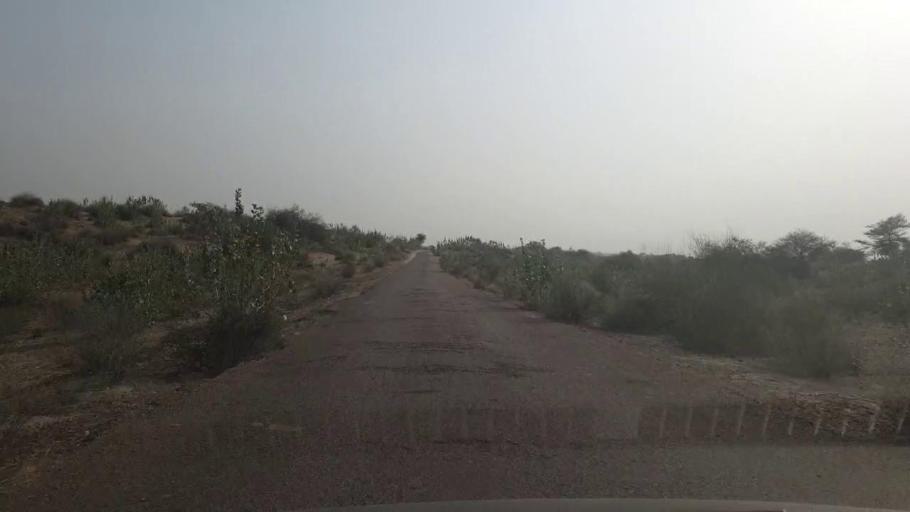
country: PK
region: Sindh
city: Chor
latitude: 25.4764
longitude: 69.9728
